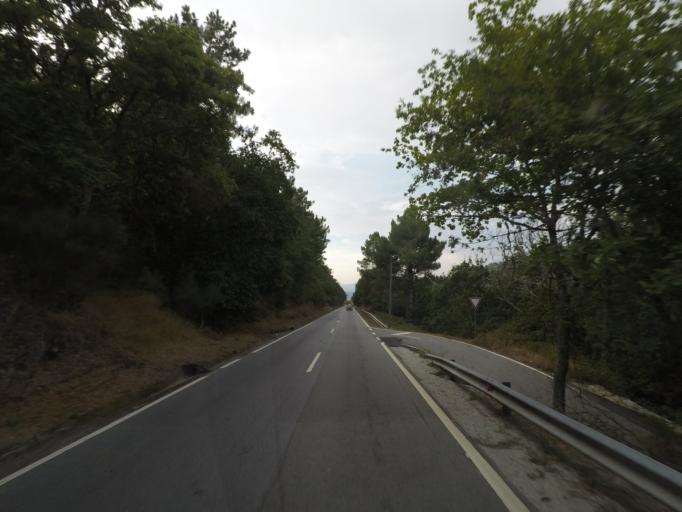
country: PT
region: Porto
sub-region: Baiao
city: Baiao
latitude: 41.2209
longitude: -7.9910
